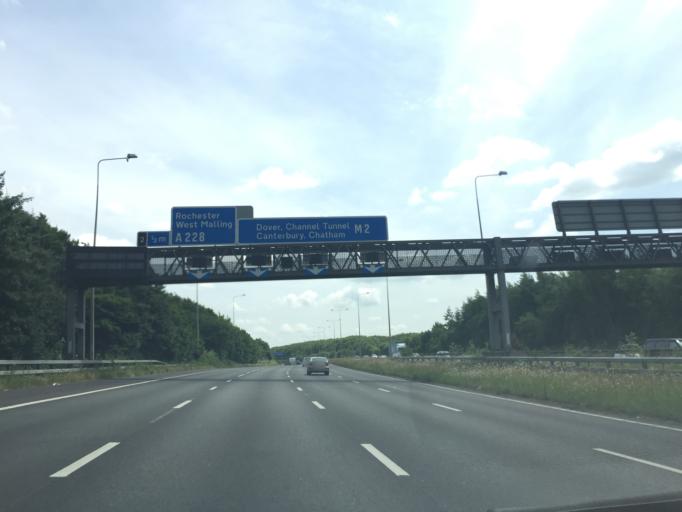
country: GB
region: England
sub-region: Medway
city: Cuxton
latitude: 51.3969
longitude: 0.4535
